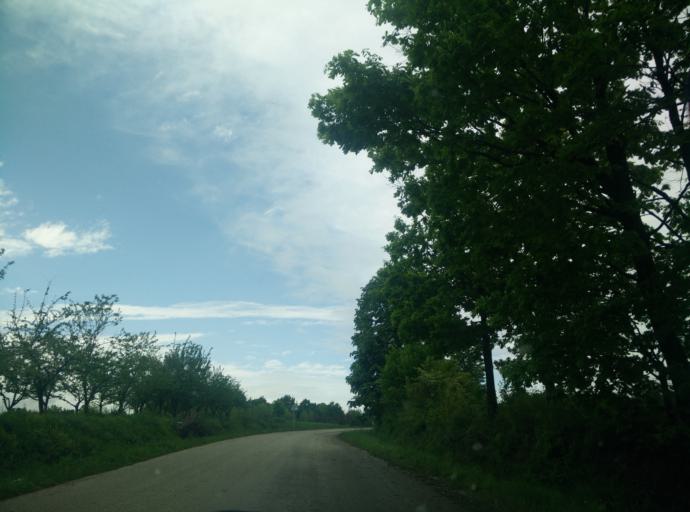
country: BA
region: Brcko
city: Brcko
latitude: 44.7841
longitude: 18.8164
